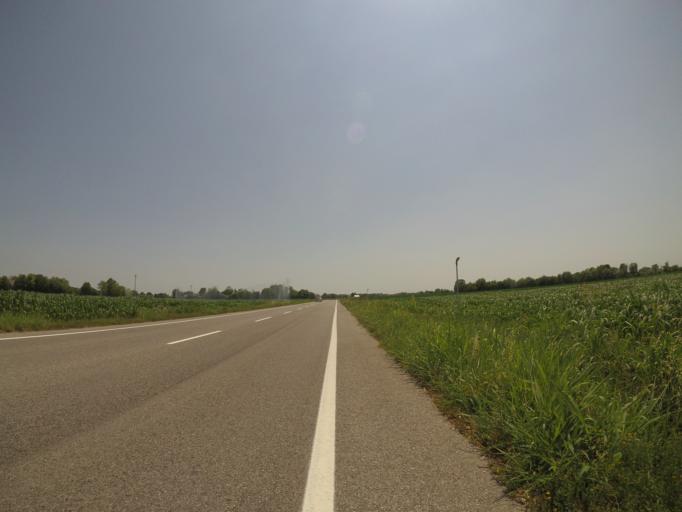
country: IT
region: Friuli Venezia Giulia
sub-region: Provincia di Udine
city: Varmo
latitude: 45.9035
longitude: 13.0045
